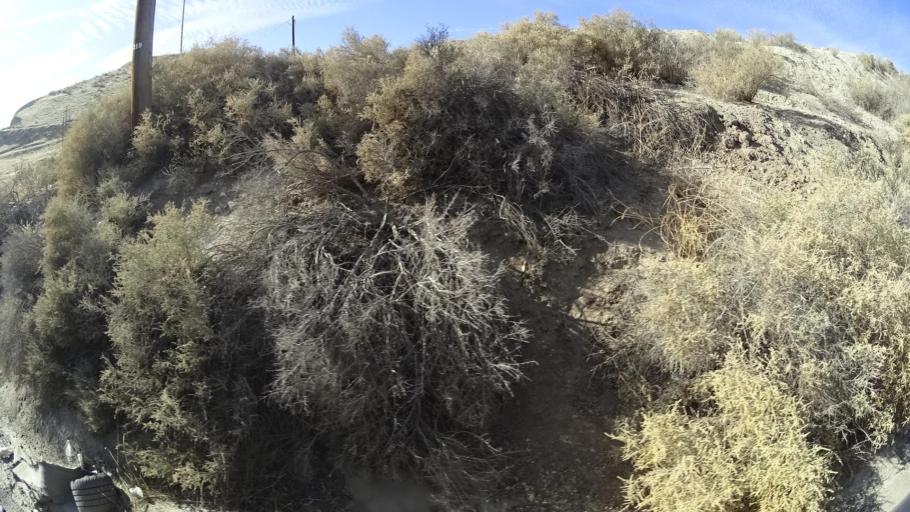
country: US
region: California
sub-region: Kern County
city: Oildale
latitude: 35.5774
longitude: -118.9605
